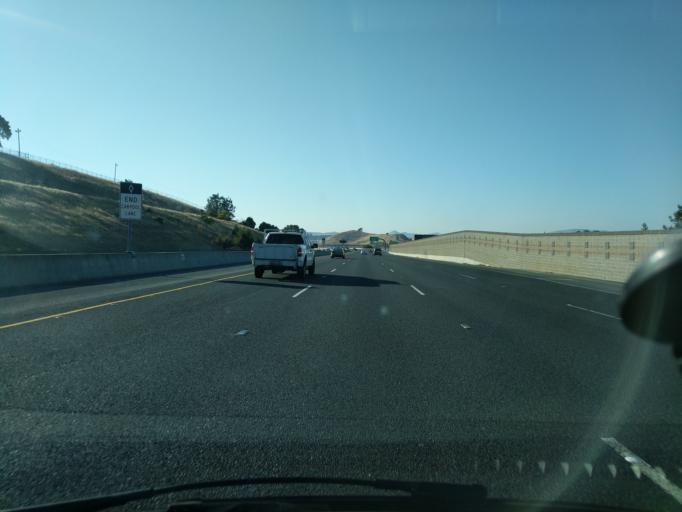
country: US
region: California
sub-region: Contra Costa County
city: Vine Hill
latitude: 38.0158
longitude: -122.0932
